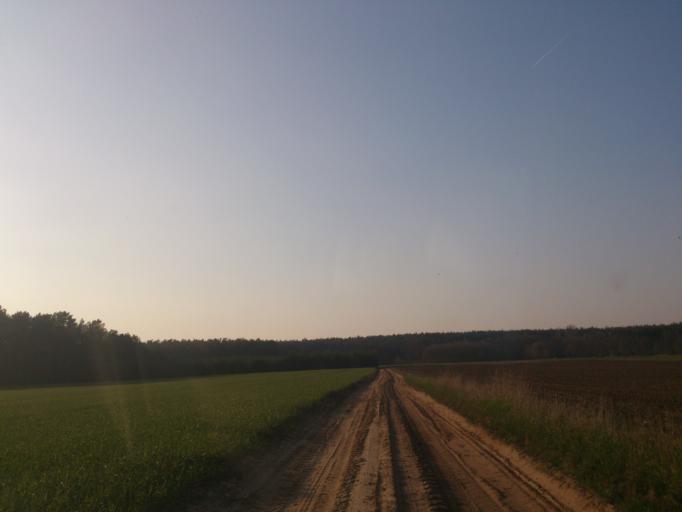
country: PL
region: Kujawsko-Pomorskie
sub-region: Powiat golubsko-dobrzynski
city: Radomin
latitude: 53.1280
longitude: 19.1333
